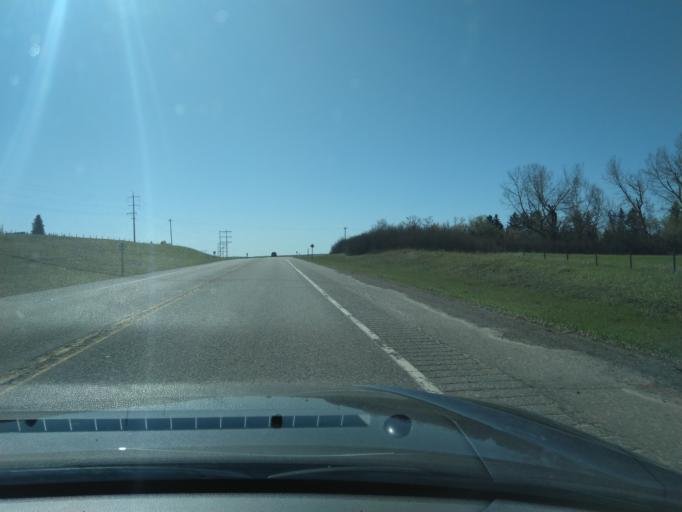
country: CA
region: Alberta
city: Cochrane
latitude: 51.0219
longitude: -114.3293
